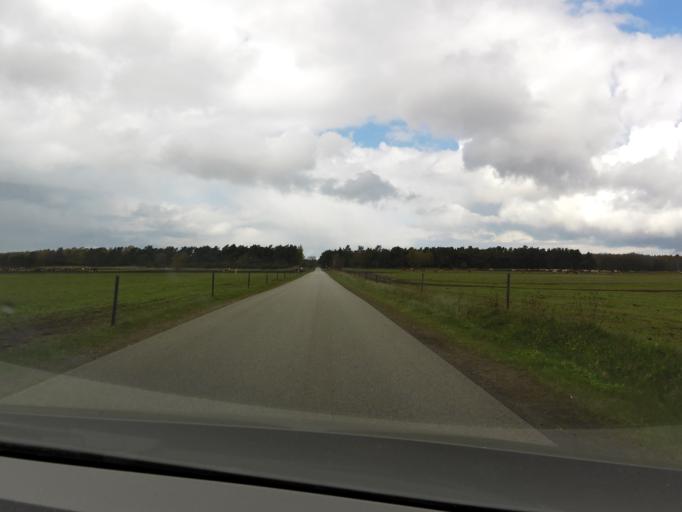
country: DE
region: Mecklenburg-Vorpommern
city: Born
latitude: 54.3901
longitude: 12.4982
